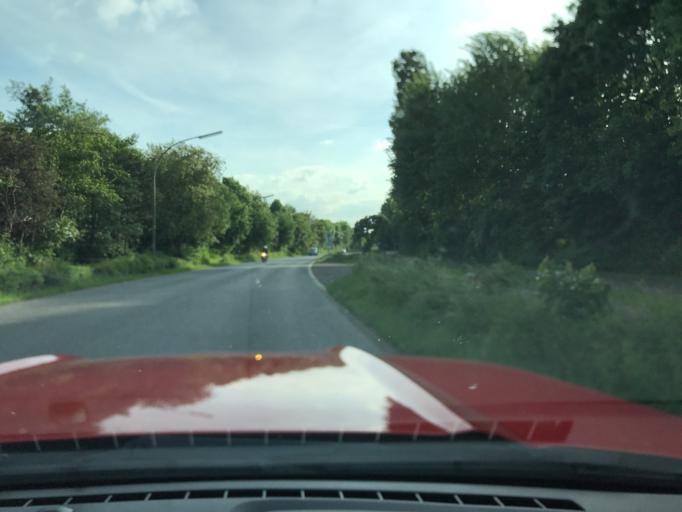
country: DE
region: North Rhine-Westphalia
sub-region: Regierungsbezirk Koln
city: Bilderstoeckchen
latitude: 51.0207
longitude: 6.9342
